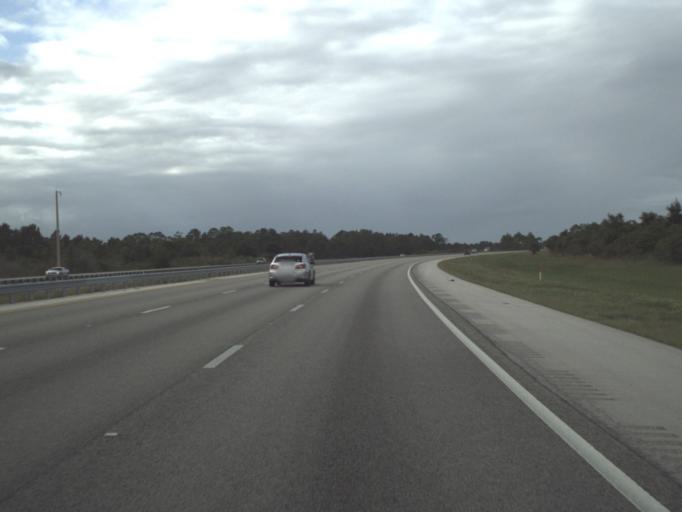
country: US
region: Florida
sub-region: Lee County
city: Suncoast Estates
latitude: 26.7578
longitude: -81.8709
